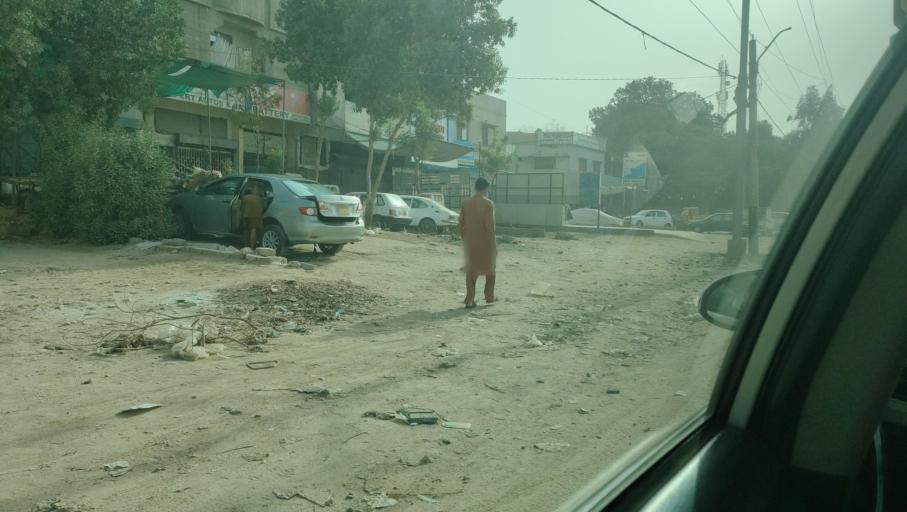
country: PK
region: Sindh
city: Malir Cantonment
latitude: 24.9350
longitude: 67.1731
